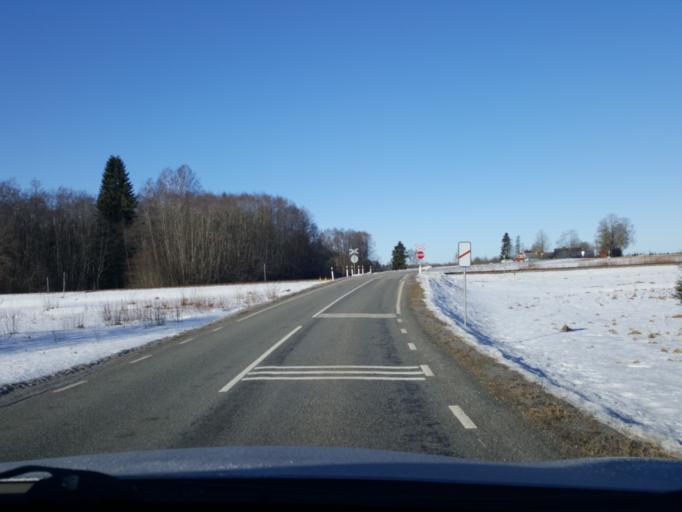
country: EE
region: Viljandimaa
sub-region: Viljandi linn
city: Viljandi
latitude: 58.4075
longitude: 25.5645
